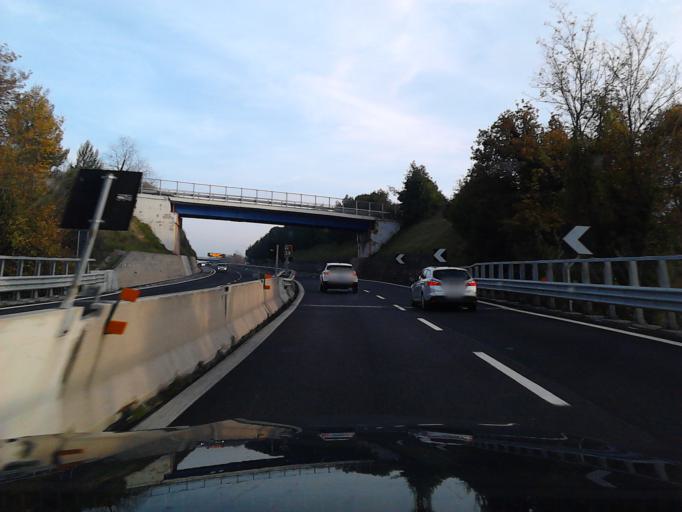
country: IT
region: Abruzzo
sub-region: Provincia di Chieti
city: Ortona
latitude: 42.3380
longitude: 14.3604
